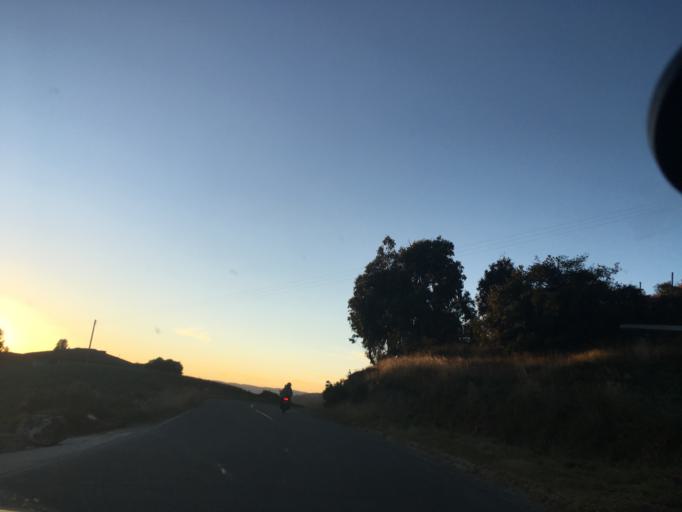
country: CO
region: Boyaca
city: Aquitania
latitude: 5.5709
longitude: -72.8928
